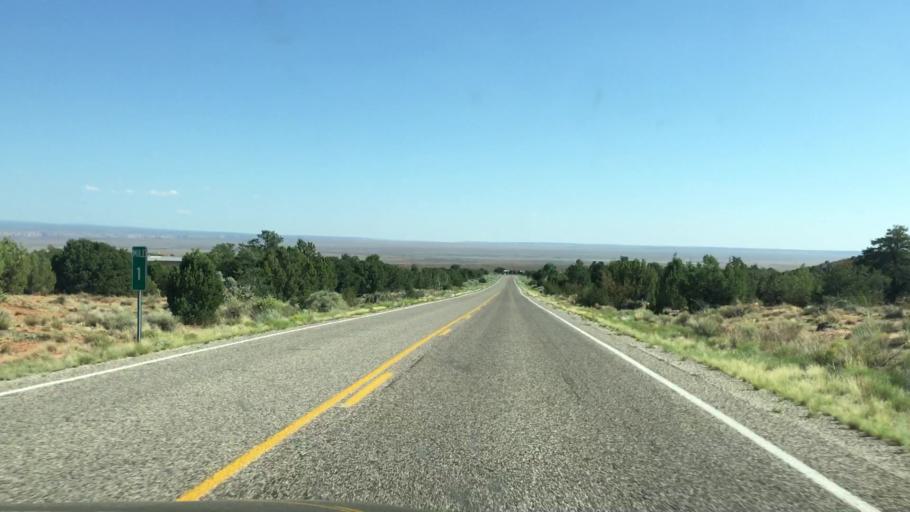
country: US
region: Arizona
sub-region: Coconino County
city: Fredonia
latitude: 36.8718
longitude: -112.7381
